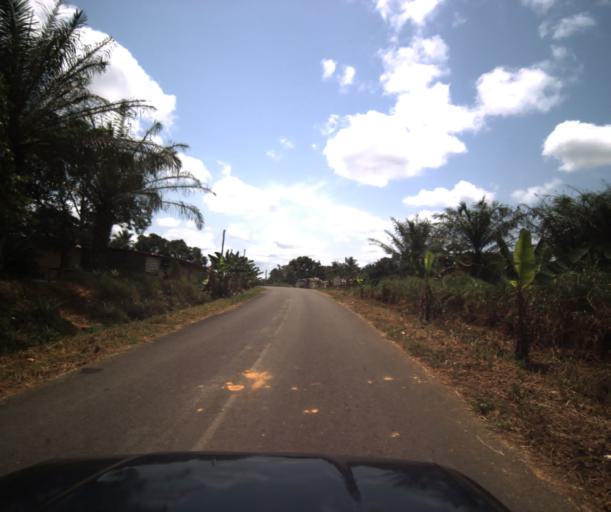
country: CM
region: Centre
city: Eseka
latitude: 3.7024
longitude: 10.7869
